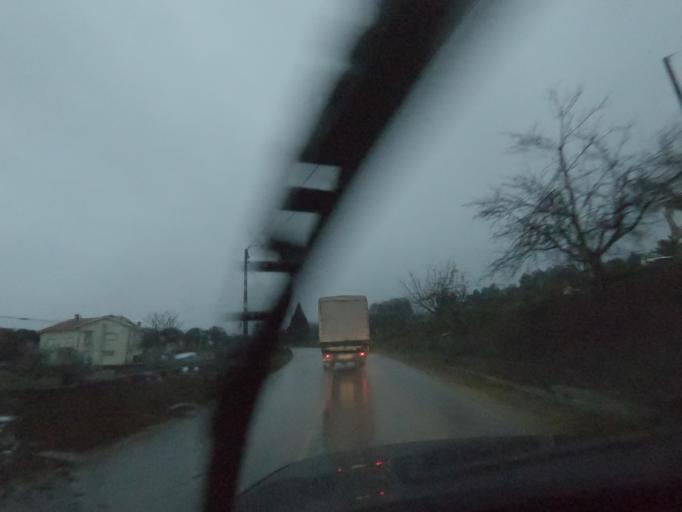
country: PT
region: Vila Real
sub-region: Sabrosa
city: Sabrosa
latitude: 41.2414
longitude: -7.5694
